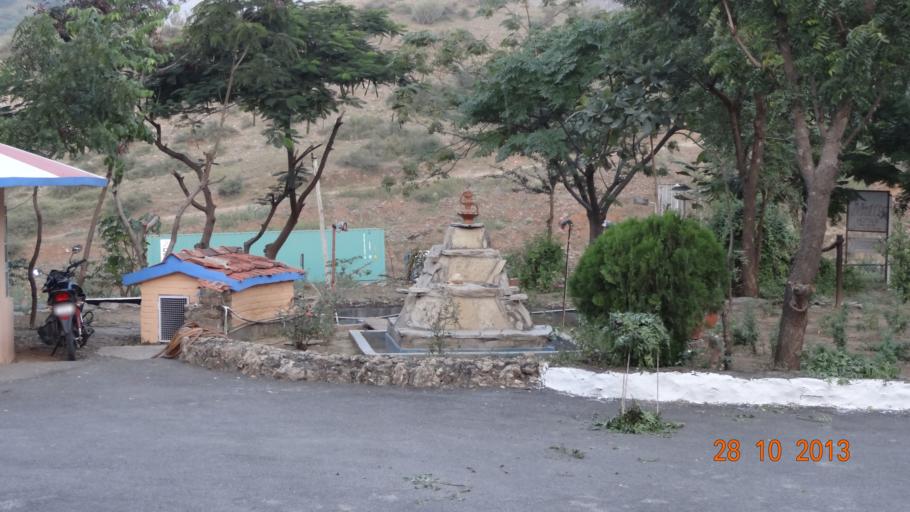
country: IN
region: Rajasthan
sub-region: Udaipur
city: Udaipur
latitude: 24.4746
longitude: 73.6501
